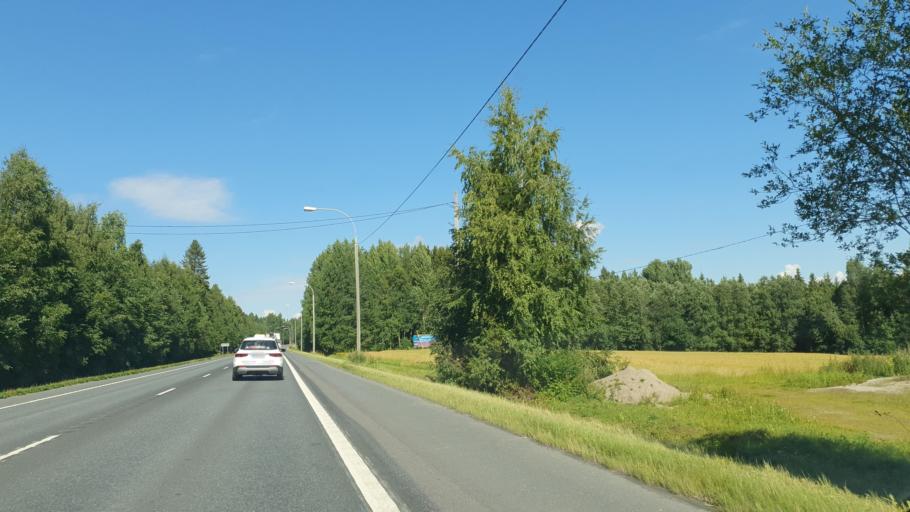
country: FI
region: Northern Savo
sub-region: Ylae-Savo
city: Iisalmi
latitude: 63.5021
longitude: 27.2628
